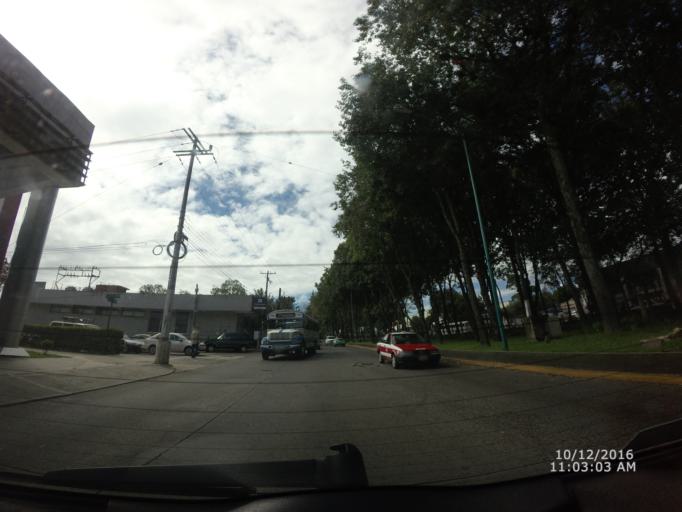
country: MX
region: Veracruz
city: Banderilla
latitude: 19.5604
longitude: -96.9284
